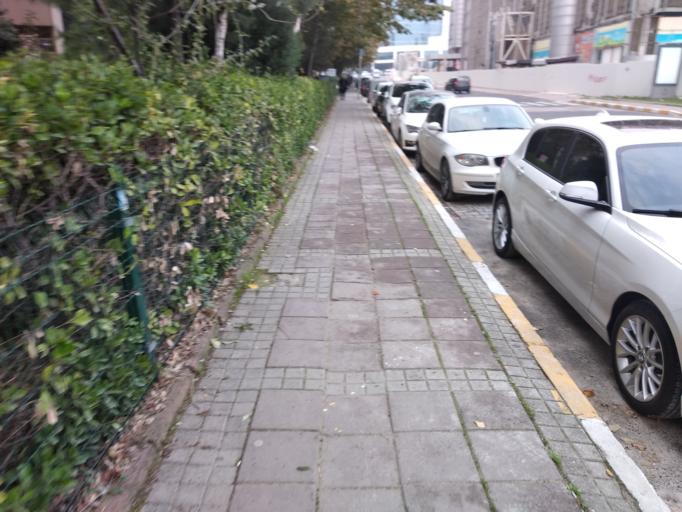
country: TR
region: Istanbul
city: Beylikduezue
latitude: 41.0115
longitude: 28.6479
